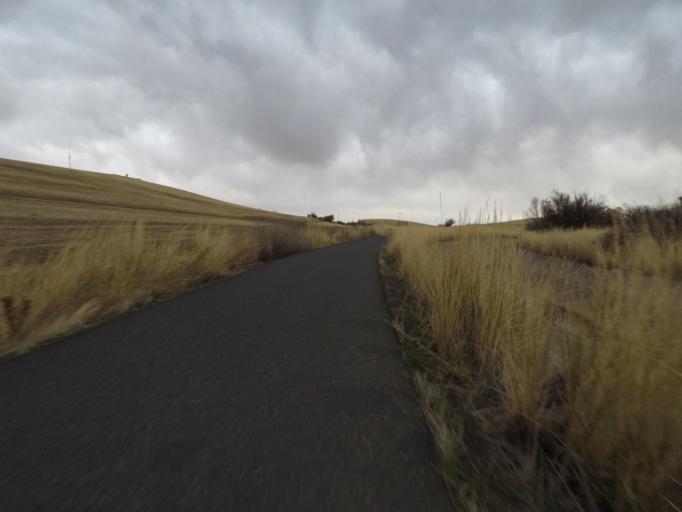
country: US
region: Washington
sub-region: Walla Walla County
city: Walla Walla East
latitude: 46.0712
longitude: -118.2706
